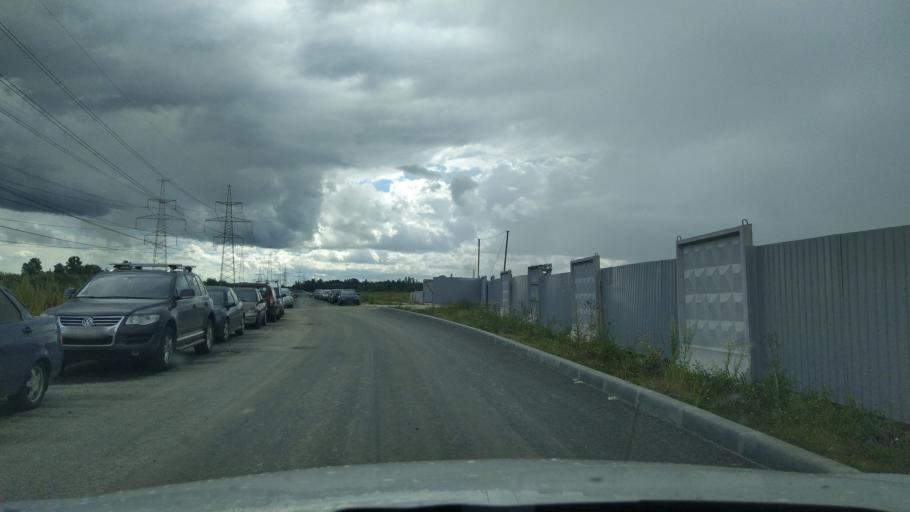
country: RU
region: St.-Petersburg
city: Krasnogvargeisky
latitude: 60.0020
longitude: 30.4828
